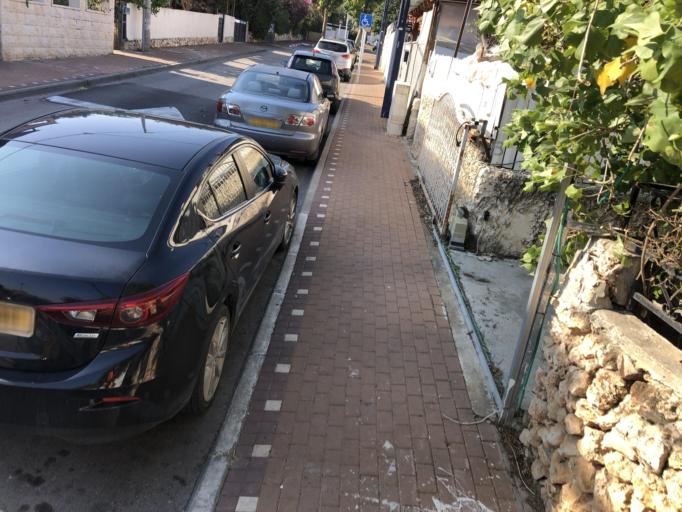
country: IL
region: Northern District
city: `Akko
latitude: 32.9260
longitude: 35.0935
